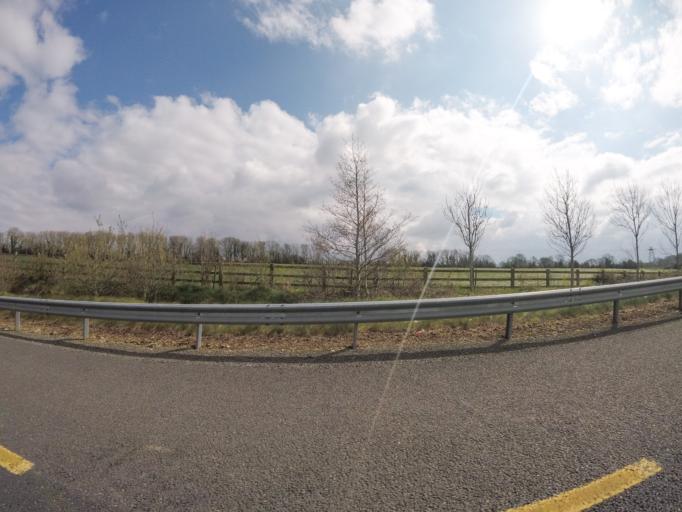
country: IE
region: Leinster
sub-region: Kilkenny
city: Mooncoin
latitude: 52.2414
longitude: -7.1893
